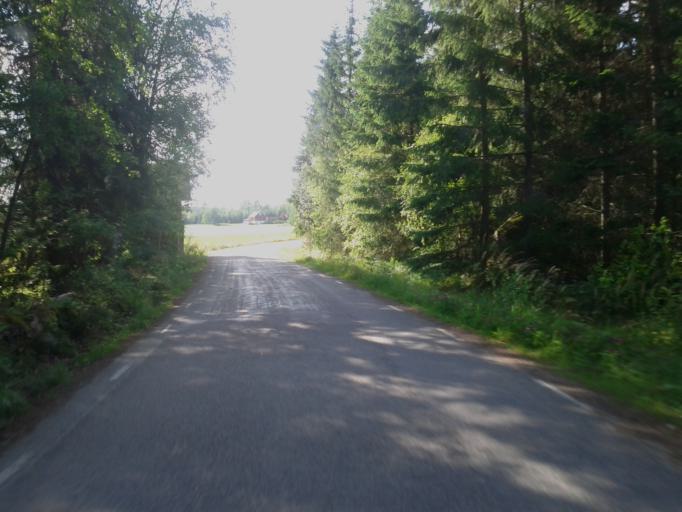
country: SE
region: Vaestmanland
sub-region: Sala Kommun
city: Sala
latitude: 59.9239
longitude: 16.4803
